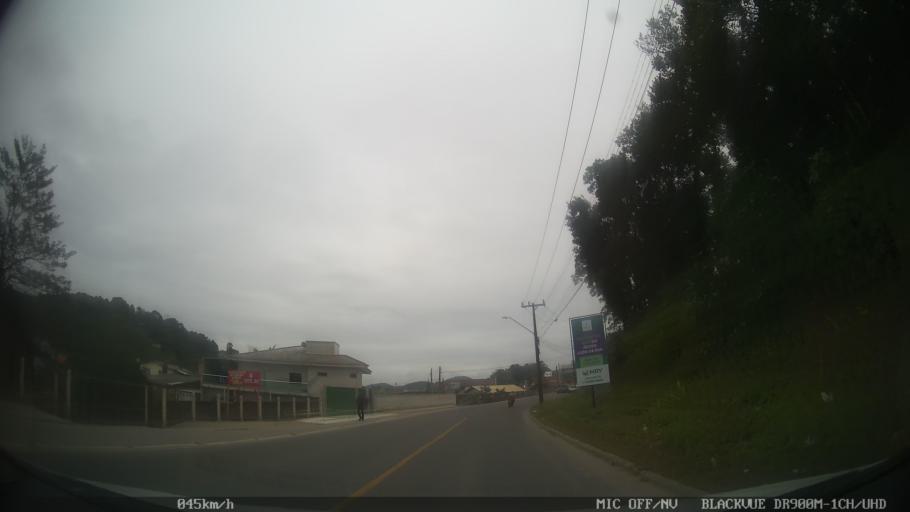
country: BR
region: Santa Catarina
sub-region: Joinville
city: Joinville
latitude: -26.3474
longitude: -48.8184
